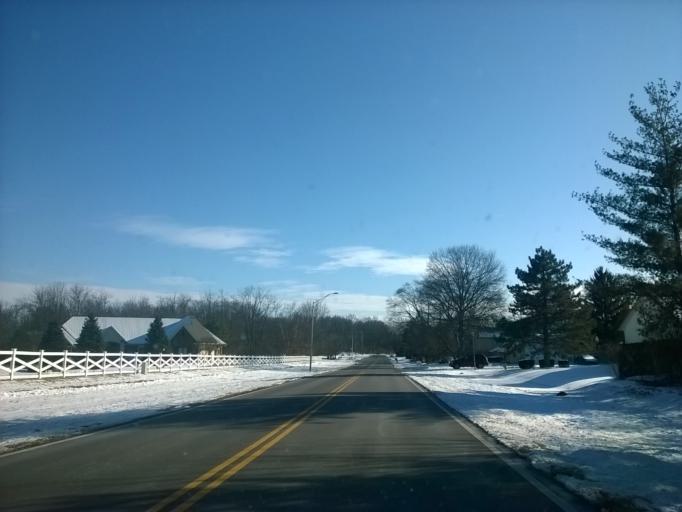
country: US
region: Indiana
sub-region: Hamilton County
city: Carmel
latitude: 39.9447
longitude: -86.0983
